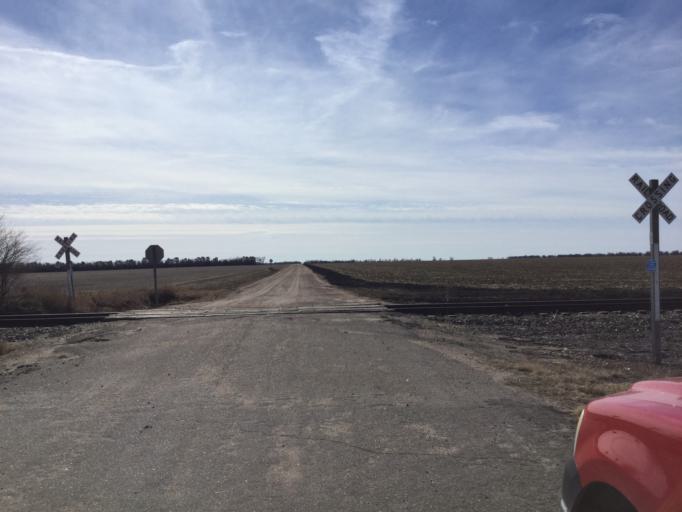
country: US
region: Kansas
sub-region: Rice County
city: Lyons
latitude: 38.5153
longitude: -98.2200
